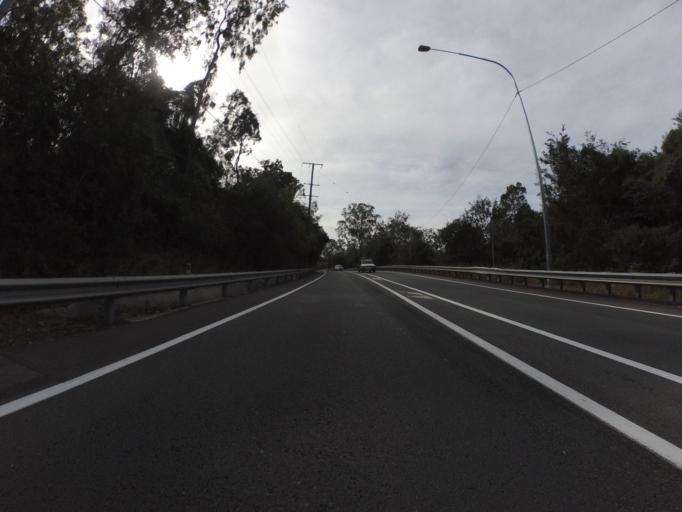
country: AU
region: Queensland
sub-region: Brisbane
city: Kenmore Hills
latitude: -27.5240
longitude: 152.9193
